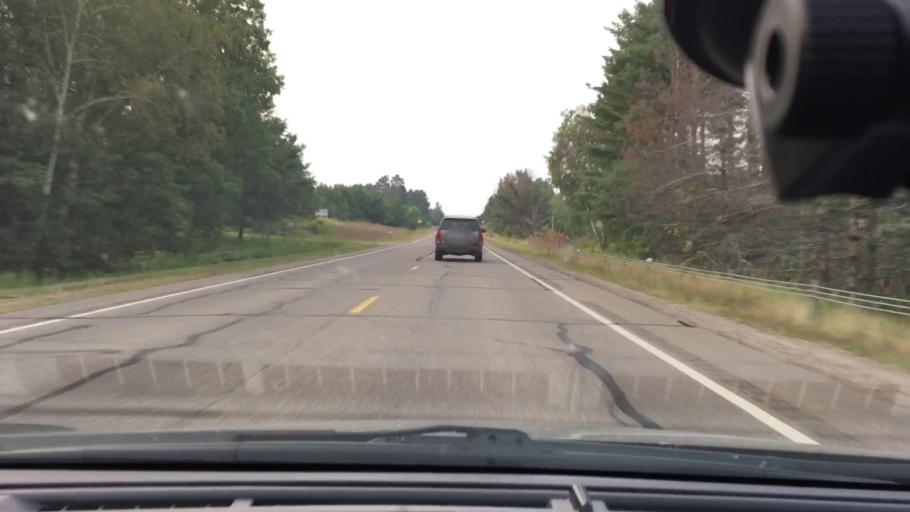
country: US
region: Minnesota
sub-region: Crow Wing County
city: Crosby
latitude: 46.4201
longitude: -93.8731
